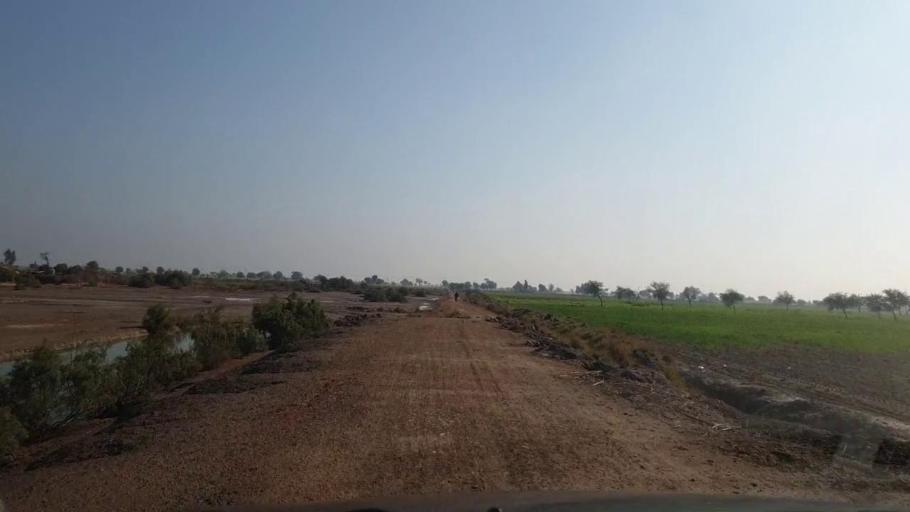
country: PK
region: Sindh
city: Sinjhoro
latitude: 26.0493
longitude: 68.7839
